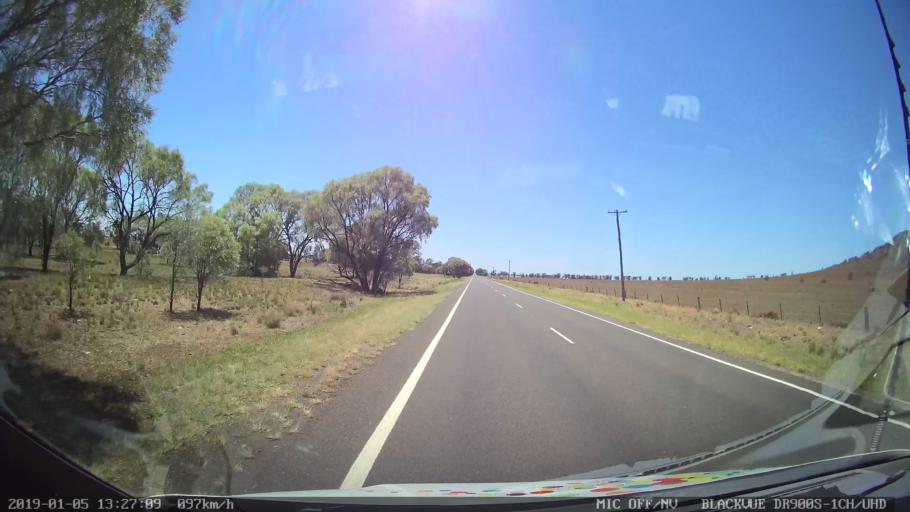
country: AU
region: New South Wales
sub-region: Gunnedah
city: Gunnedah
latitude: -31.0471
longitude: 150.0252
